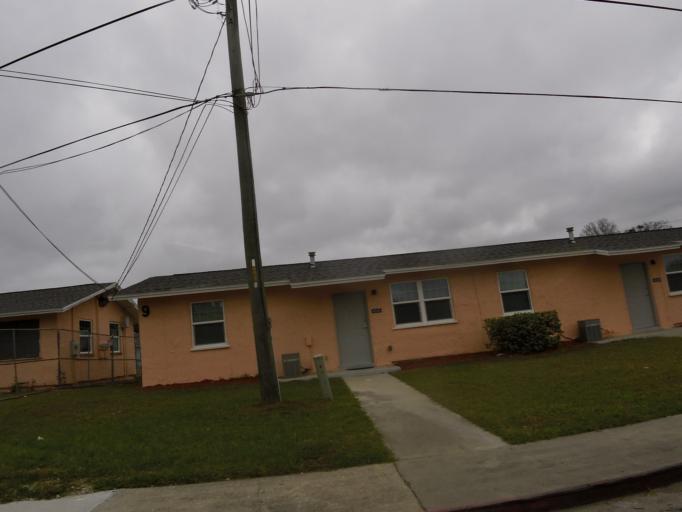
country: US
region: Florida
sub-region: Duval County
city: Jacksonville
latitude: 30.3677
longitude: -81.6837
